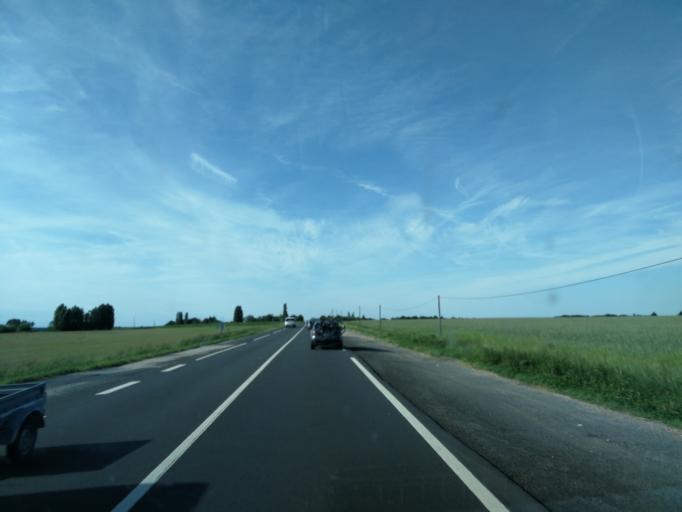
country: FR
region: Centre
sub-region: Departement du Loir-et-Cher
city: Moree
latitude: 47.9144
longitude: 1.1909
